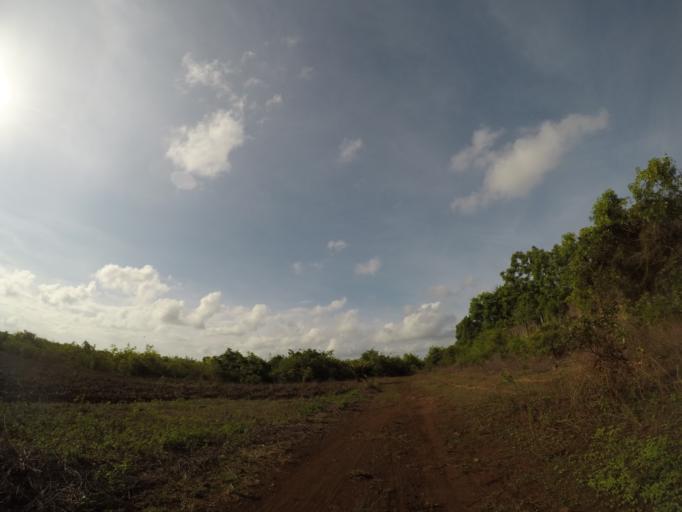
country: TZ
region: Zanzibar Central/South
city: Koani
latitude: -6.2190
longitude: 39.3078
